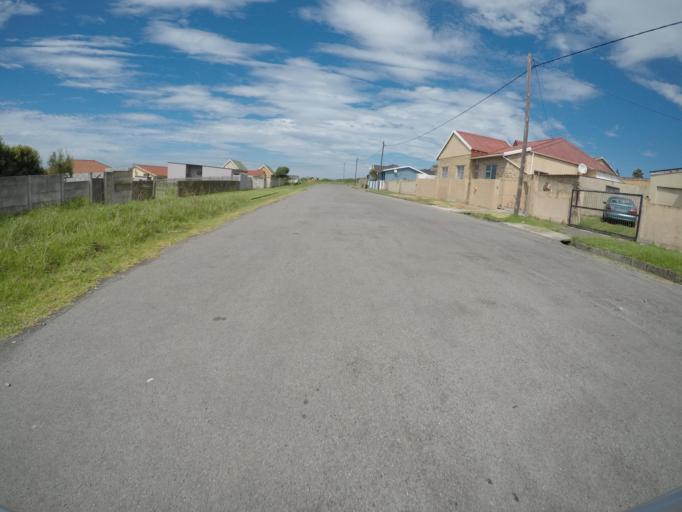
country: ZA
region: Eastern Cape
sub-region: Buffalo City Metropolitan Municipality
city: East London
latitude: -33.0378
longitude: 27.9043
